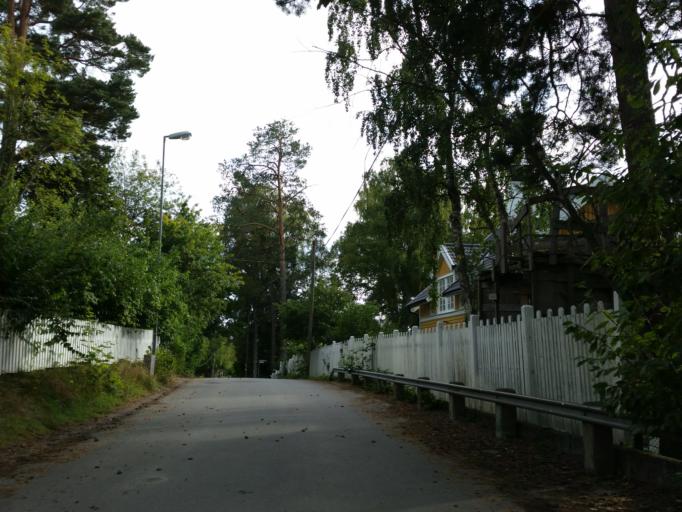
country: SE
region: Stockholm
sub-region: Sollentuna Kommun
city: Sollentuna
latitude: 59.4615
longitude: 17.9257
